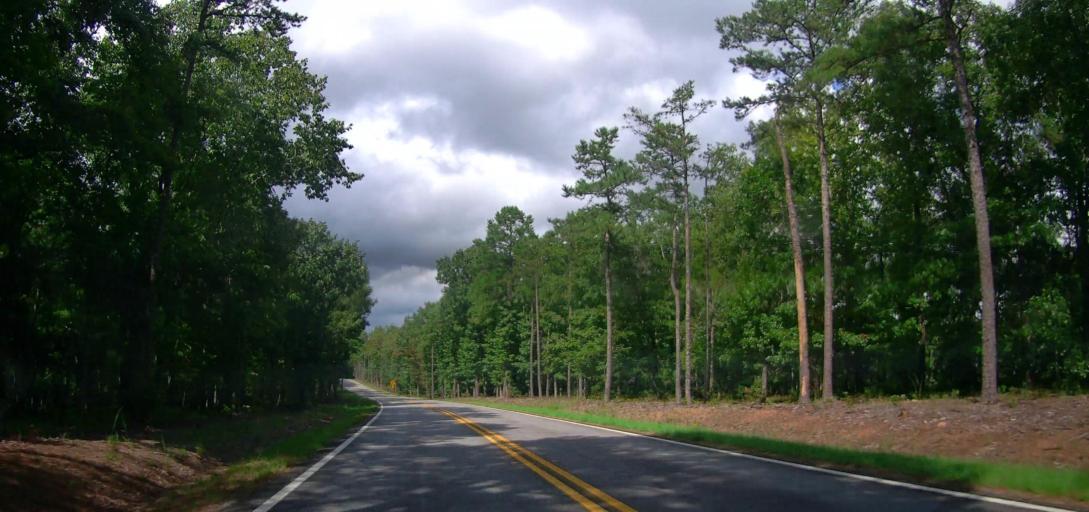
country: US
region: Georgia
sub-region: Harris County
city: Pine Mountain
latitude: 32.8508
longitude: -84.7469
